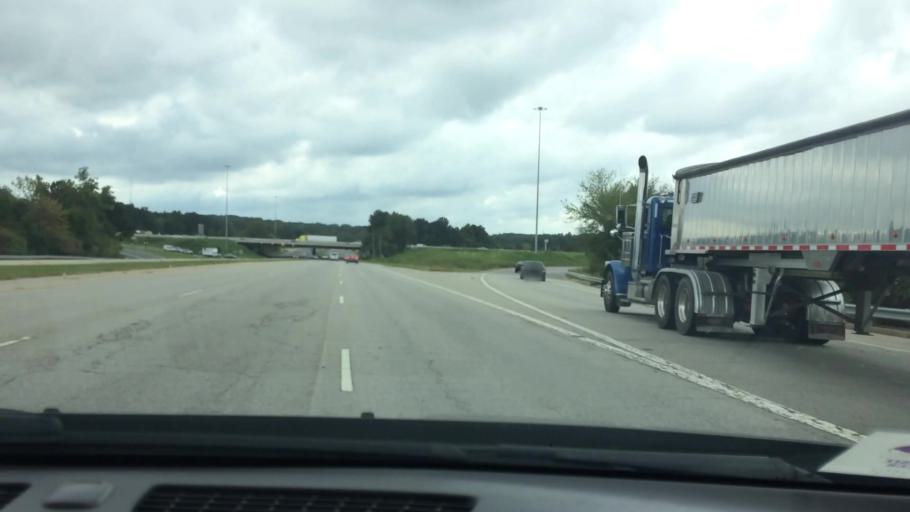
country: US
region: North Carolina
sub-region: Wake County
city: Raleigh
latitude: 35.7579
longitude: -78.6352
